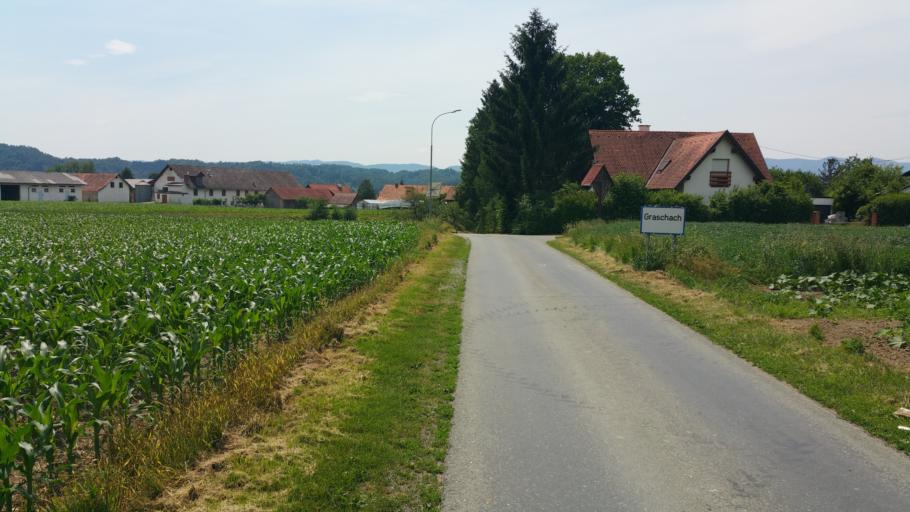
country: AT
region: Styria
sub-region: Politischer Bezirk Deutschlandsberg
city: Sankt Martin im Sulmtal
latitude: 46.7528
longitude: 15.3296
